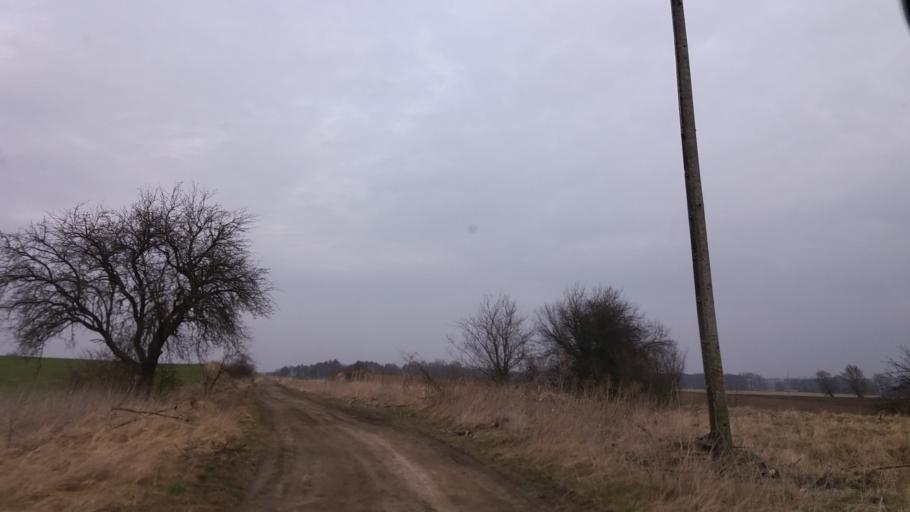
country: PL
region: West Pomeranian Voivodeship
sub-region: Powiat choszczenski
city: Pelczyce
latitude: 53.1057
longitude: 15.3334
